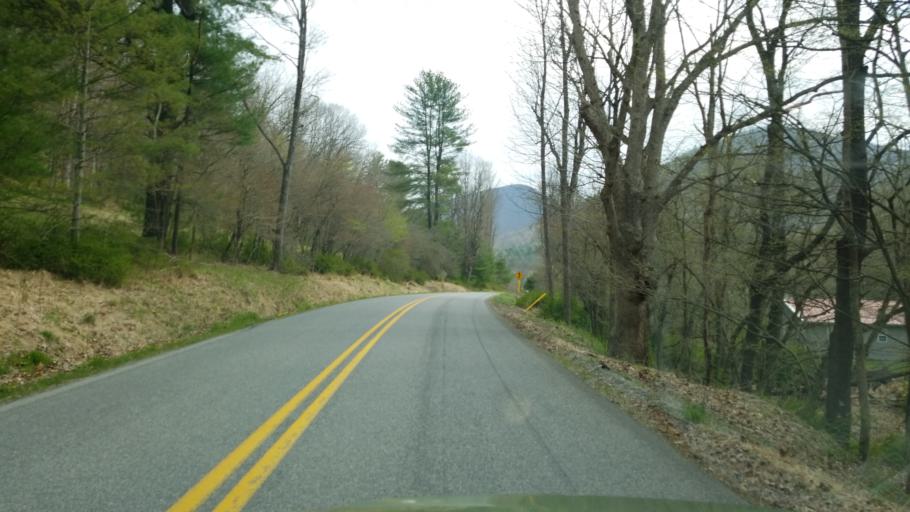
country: US
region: Pennsylvania
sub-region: Cameron County
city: Emporium
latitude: 41.3108
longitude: -78.0866
